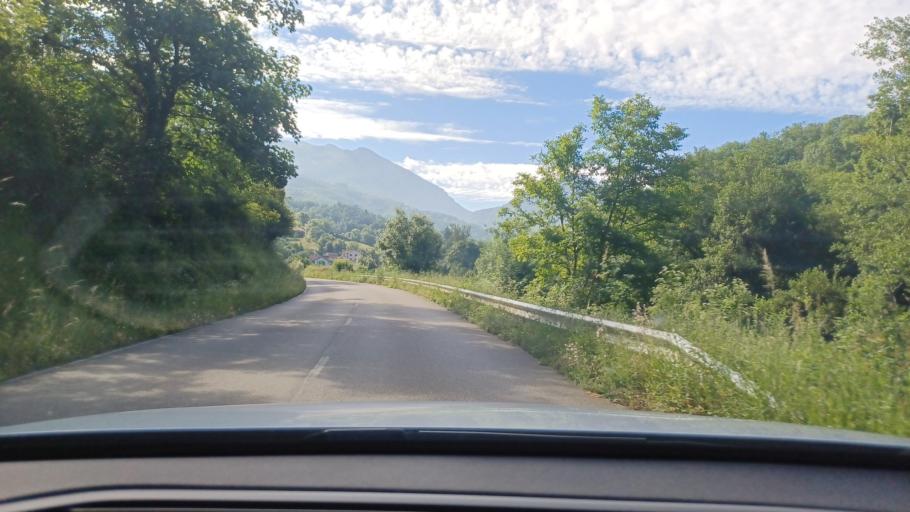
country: ES
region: Asturias
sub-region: Province of Asturias
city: La Plaza
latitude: 43.1490
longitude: -6.0901
